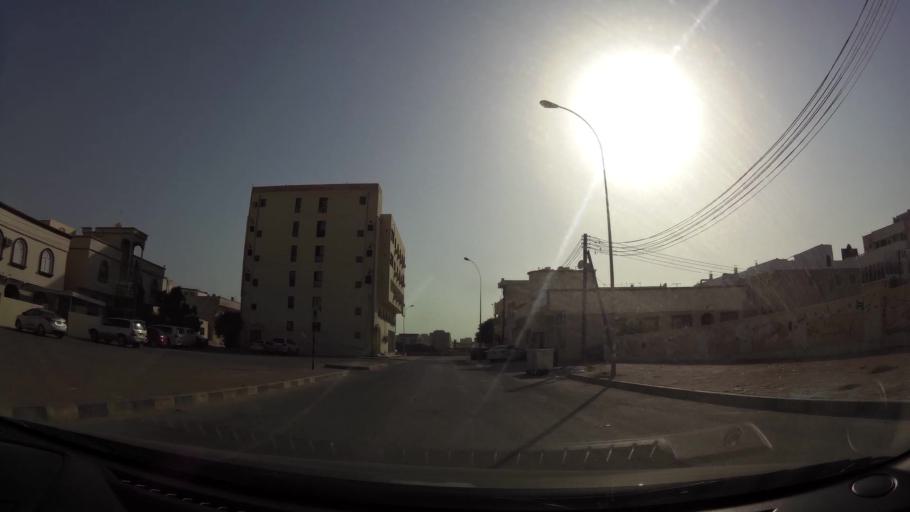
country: OM
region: Zufar
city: Salalah
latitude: 17.0062
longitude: 54.0696
